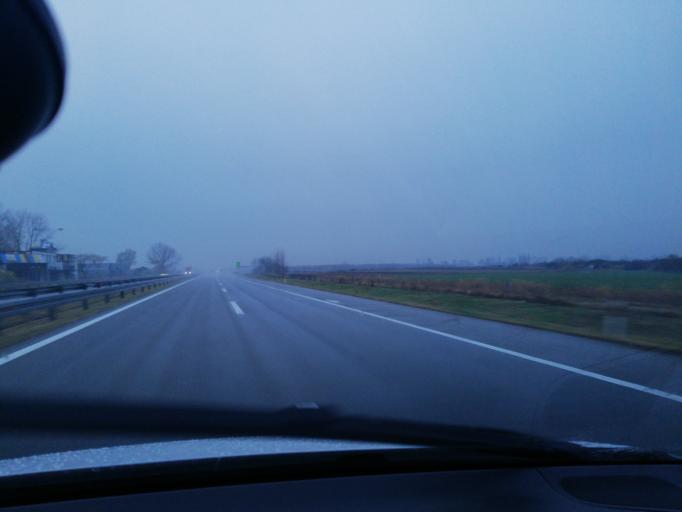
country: RS
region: Autonomna Pokrajina Vojvodina
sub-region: Sremski Okrug
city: Sremska Mitrovica
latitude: 45.0012
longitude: 19.6273
